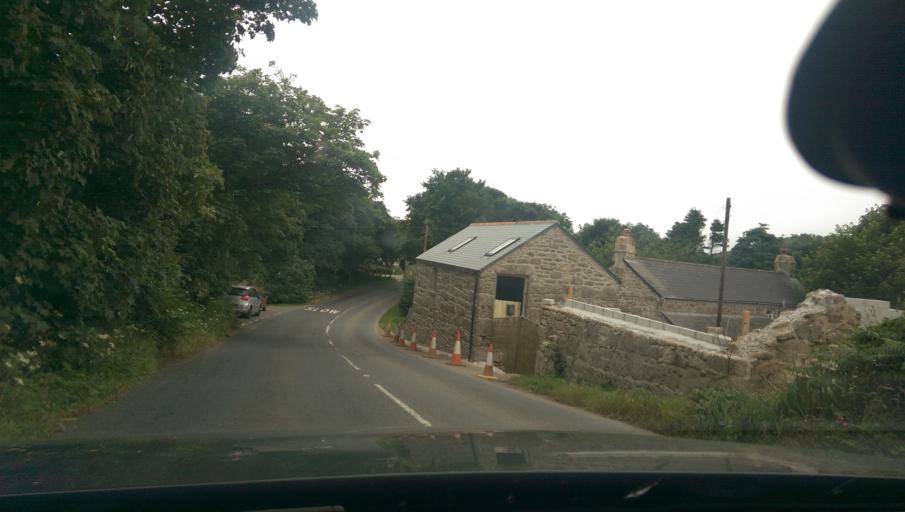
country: GB
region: England
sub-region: Cornwall
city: St. Buryan
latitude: 50.0916
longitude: -5.6255
